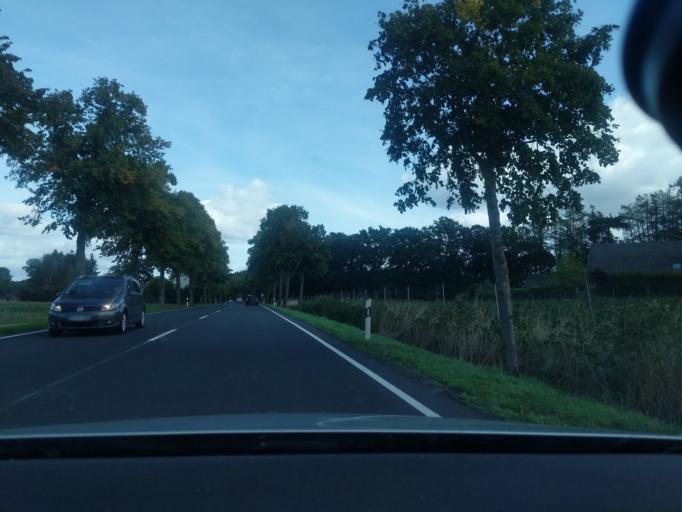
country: DE
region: Lower Saxony
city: Belm
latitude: 52.3277
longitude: 8.1629
